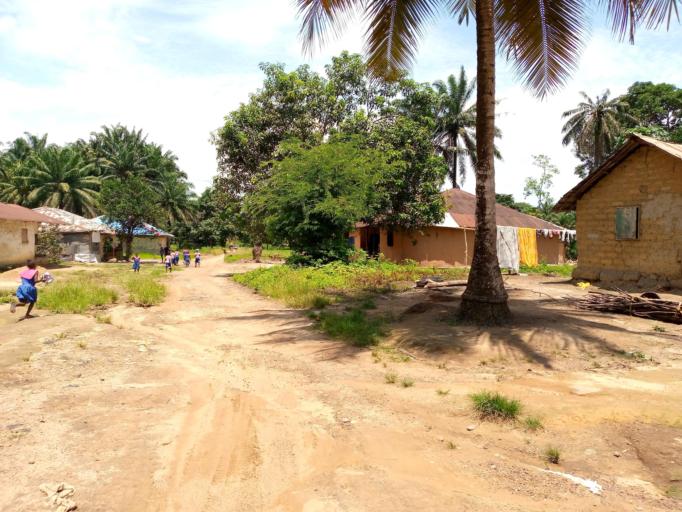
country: SL
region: Northern Province
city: Magburaka
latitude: 8.7102
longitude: -11.9594
